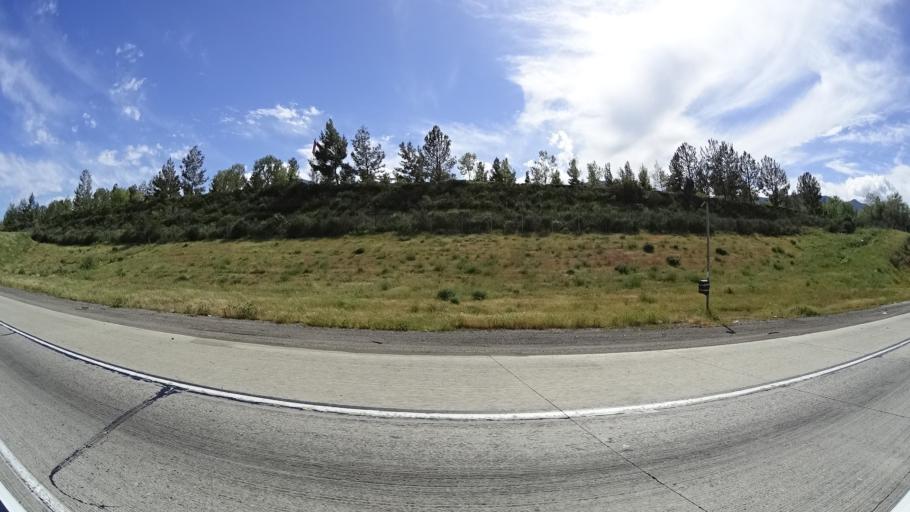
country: US
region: California
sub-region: Riverside County
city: El Cerrito
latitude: 33.7596
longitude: -117.4659
